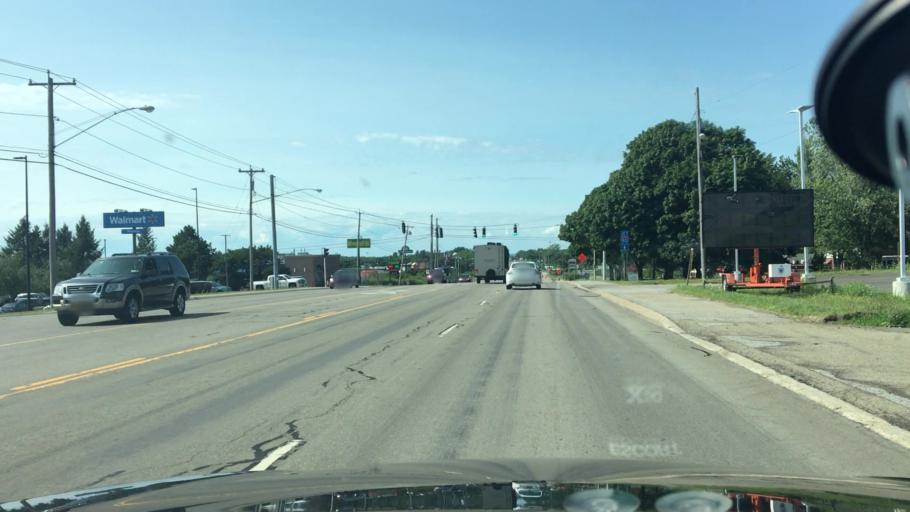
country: US
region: New York
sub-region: Chautauqua County
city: Fredonia
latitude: 42.4542
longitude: -79.3098
